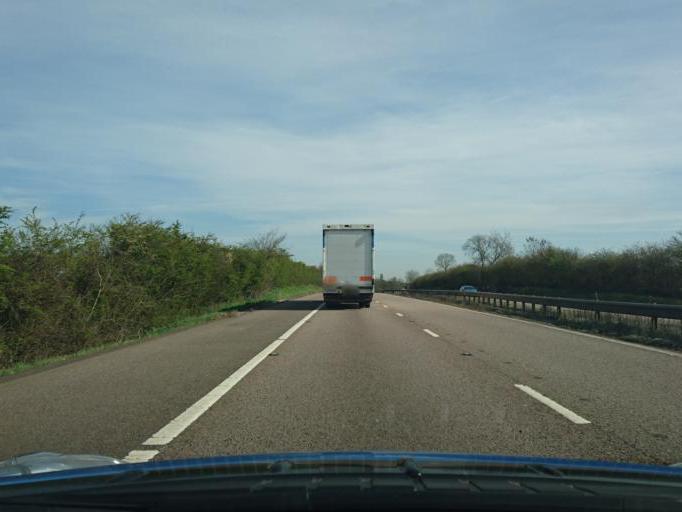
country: GB
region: England
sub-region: Worcestershire
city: Upton upon Severn
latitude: 52.0115
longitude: -2.2377
